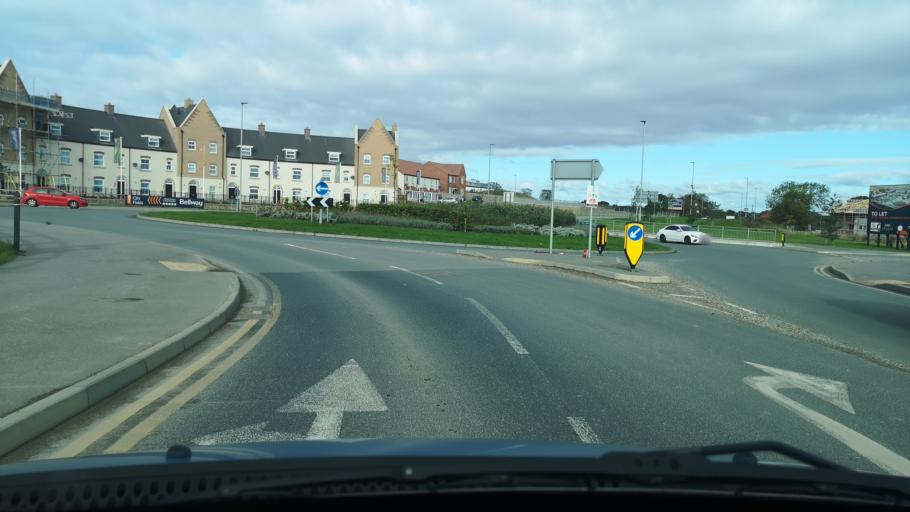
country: GB
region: England
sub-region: City and Borough of Wakefield
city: Wakefield
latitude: 53.6965
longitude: -1.4789
